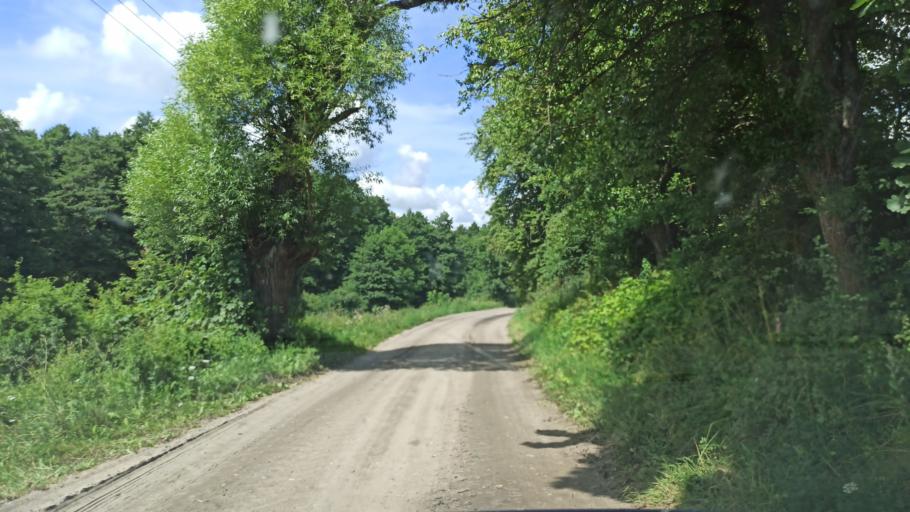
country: PL
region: Warmian-Masurian Voivodeship
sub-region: Powiat ostrodzki
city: Morag
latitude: 53.8639
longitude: 20.0576
